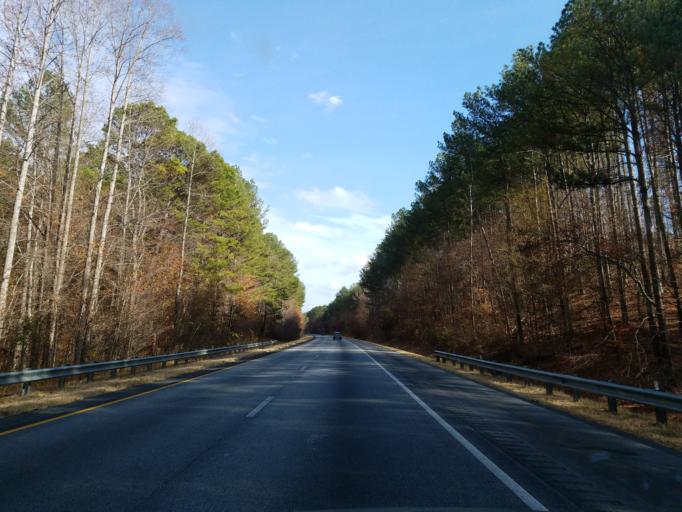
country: US
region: Alabama
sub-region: Cleburne County
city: Heflin
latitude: 33.6185
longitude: -85.6431
